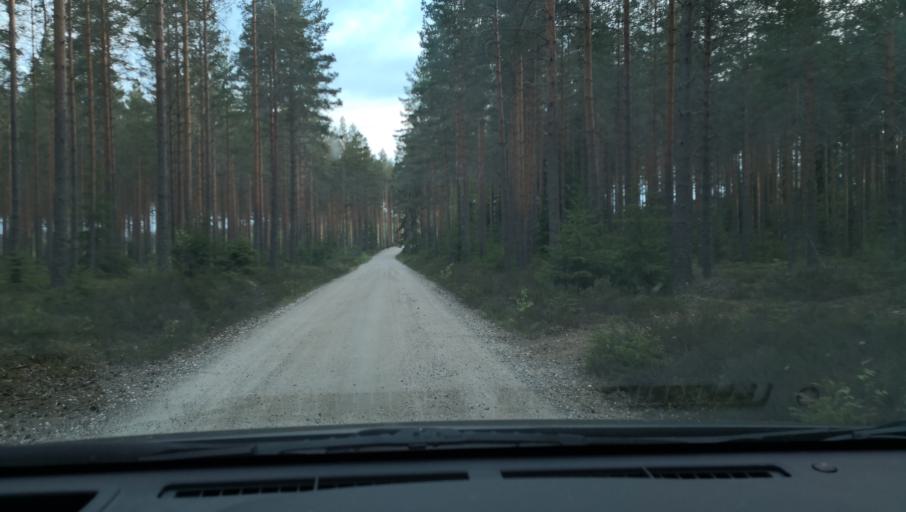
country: SE
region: Vaestmanland
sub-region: Skinnskattebergs Kommun
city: Skinnskatteberg
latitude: 59.7999
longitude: 15.4911
